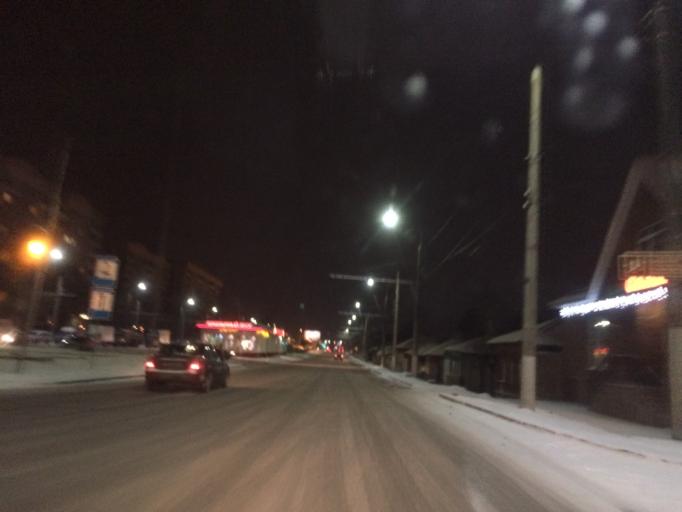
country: RU
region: Tula
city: Tula
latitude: 54.2033
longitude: 37.6390
